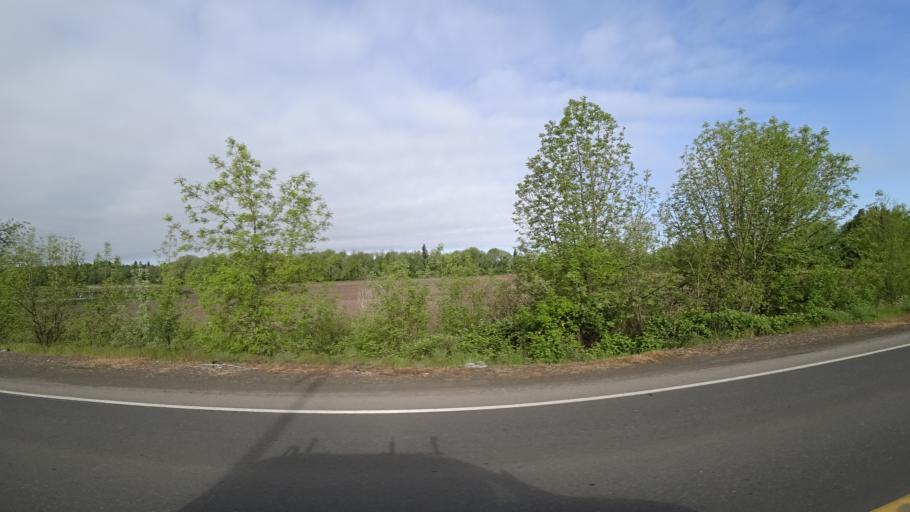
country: US
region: Oregon
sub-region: Washington County
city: Hillsboro
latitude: 45.4988
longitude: -122.9917
